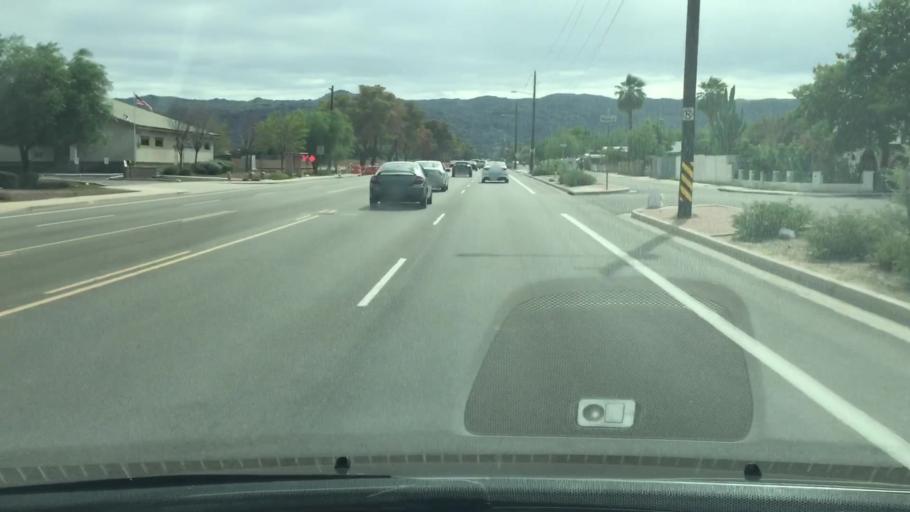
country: US
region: Arizona
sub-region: Maricopa County
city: Guadalupe
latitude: 33.3908
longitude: -112.0302
